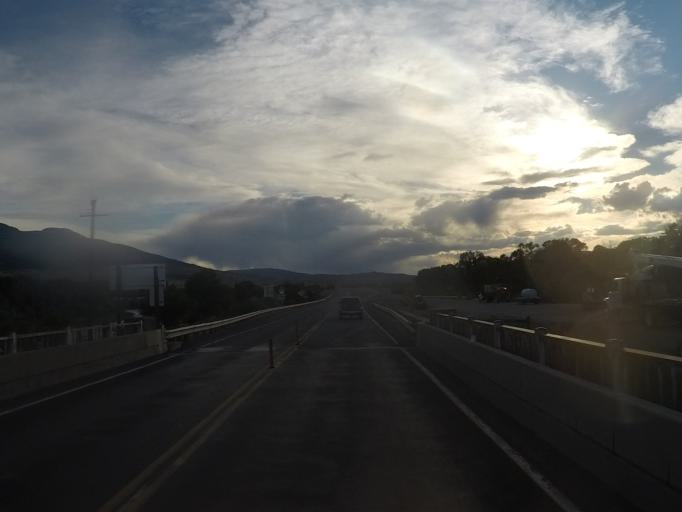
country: US
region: Montana
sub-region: Park County
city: Livingston
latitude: 45.6443
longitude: -110.5621
